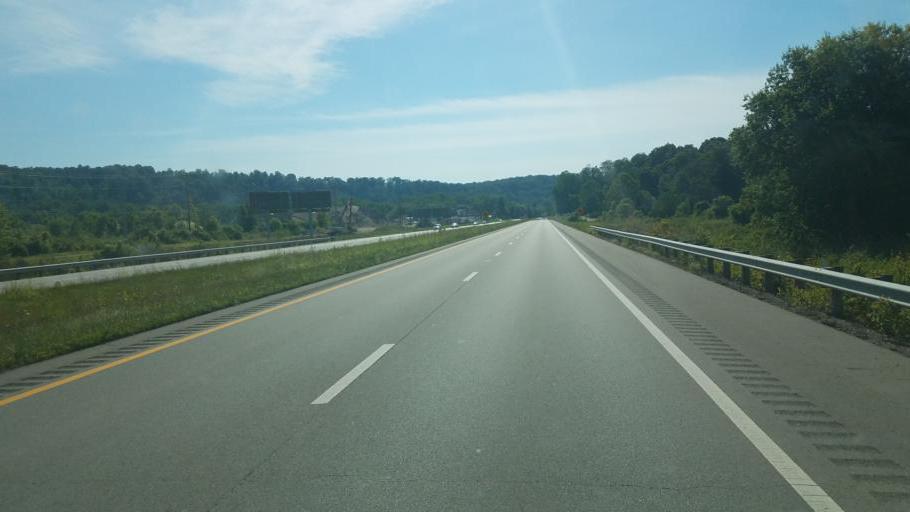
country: US
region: Ohio
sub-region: Athens County
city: Chauncey
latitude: 39.3903
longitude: -82.1494
